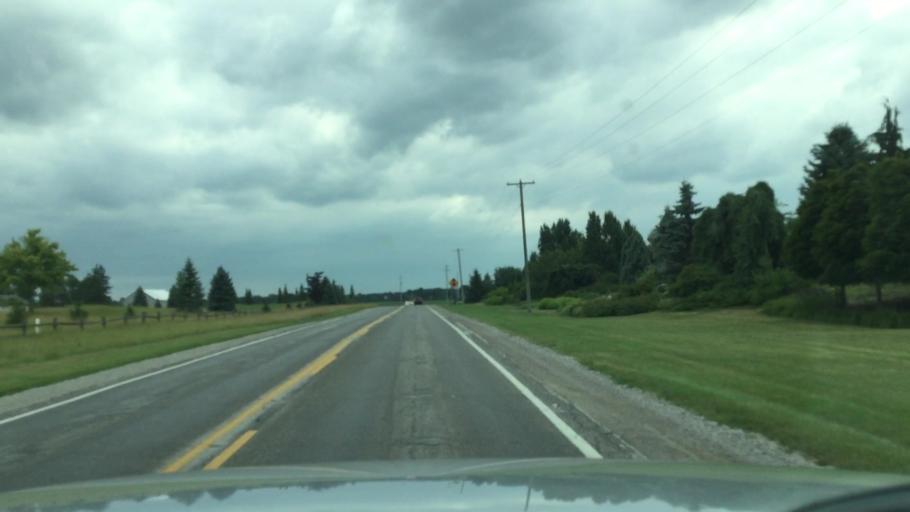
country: US
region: Michigan
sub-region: Saginaw County
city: Frankenmuth
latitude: 43.3246
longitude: -83.7581
